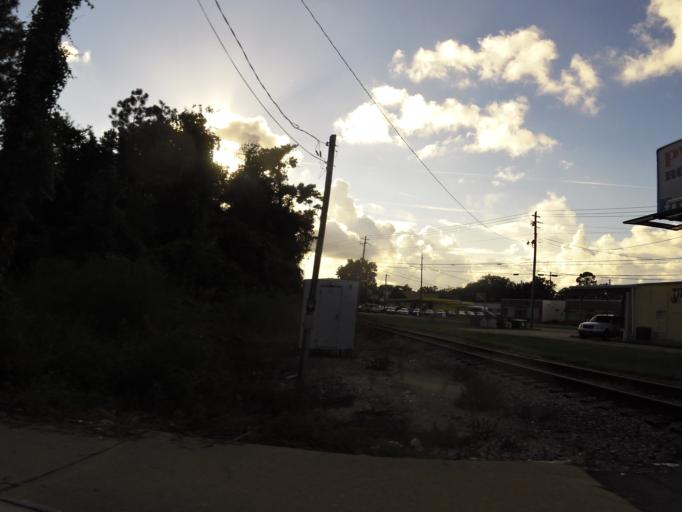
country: US
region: Georgia
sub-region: Glynn County
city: Brunswick
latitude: 31.1730
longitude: -81.4915
